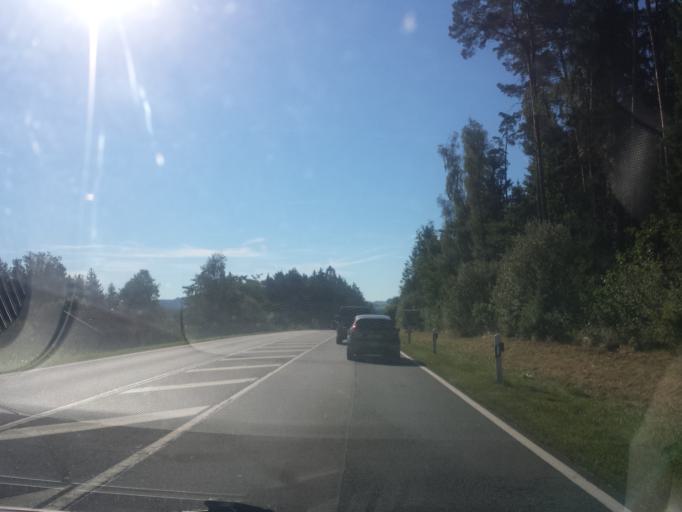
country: DE
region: Bavaria
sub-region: Lower Bavaria
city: Viechtach
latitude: 49.0650
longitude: 12.8990
